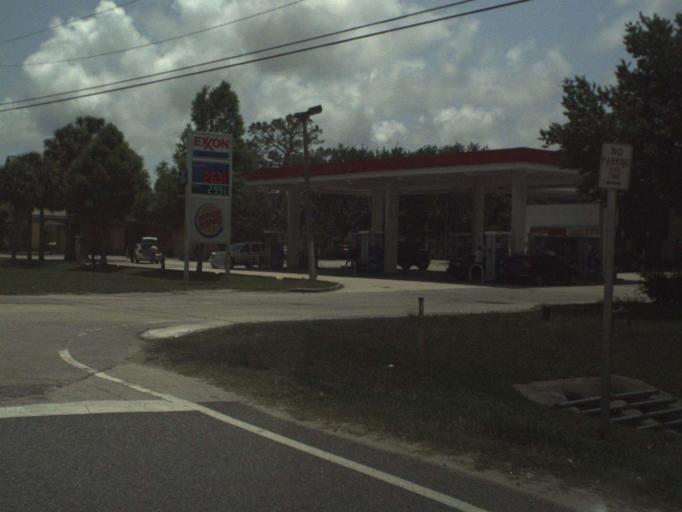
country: US
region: Florida
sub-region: Volusia County
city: Ormond-by-the-Sea
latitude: 29.3373
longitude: -81.1332
